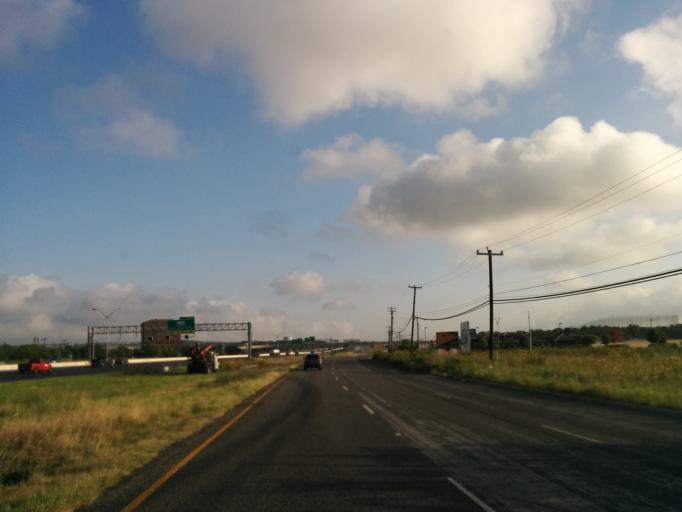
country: US
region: Texas
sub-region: Bexar County
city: Shavano Park
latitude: 29.5827
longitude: -98.5965
